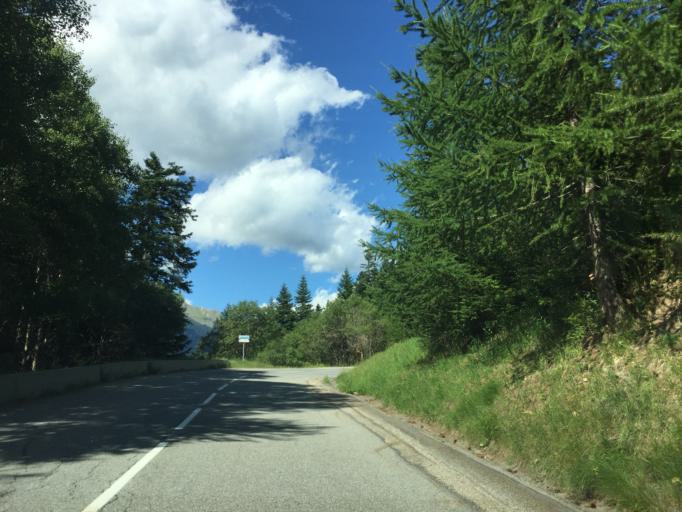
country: FR
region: Rhone-Alpes
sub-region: Departement de la Savoie
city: Modane
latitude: 45.1821
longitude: 6.6579
